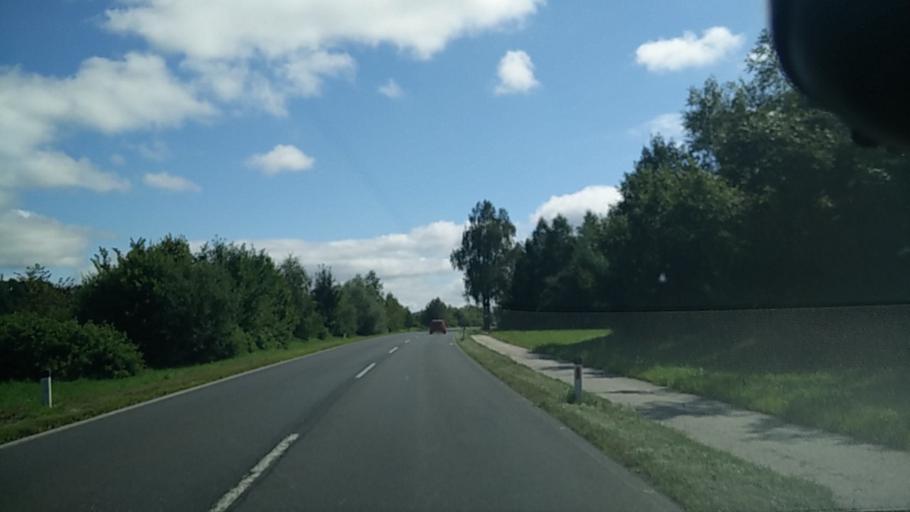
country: AT
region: Carinthia
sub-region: Politischer Bezirk Villach Land
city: Finkenstein am Faaker See
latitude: 46.5614
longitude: 13.8563
